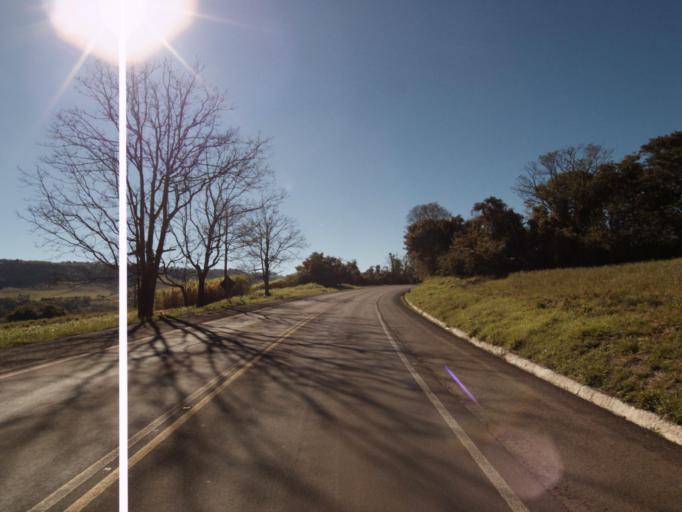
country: BR
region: Rio Grande do Sul
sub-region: Frederico Westphalen
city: Frederico Westphalen
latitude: -26.7978
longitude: -53.3270
